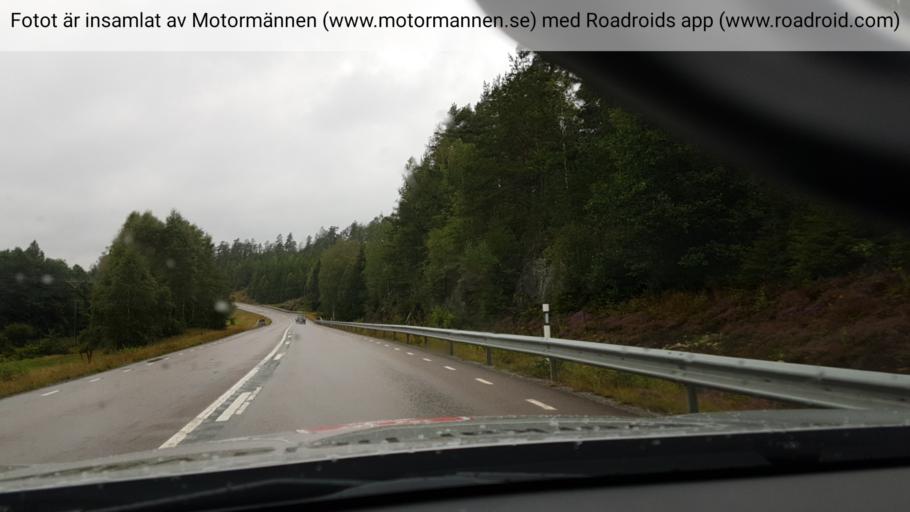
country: SE
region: Vaestra Goetaland
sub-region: Dals-Ed Kommun
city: Ed
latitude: 58.9365
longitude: 12.0712
